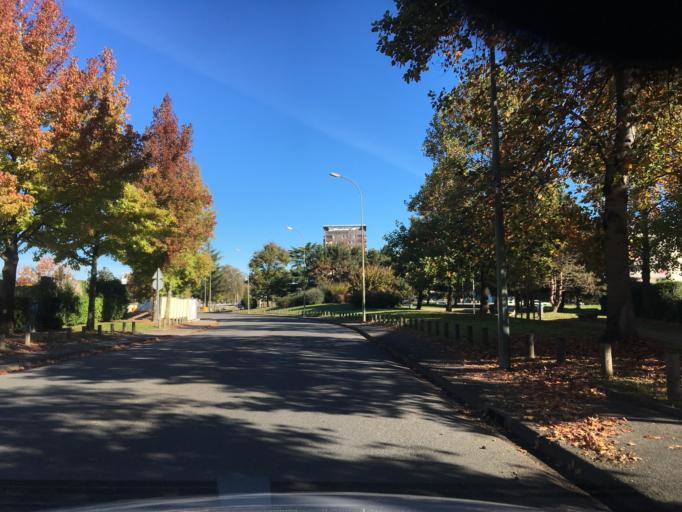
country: FR
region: Aquitaine
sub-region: Departement des Pyrenees-Atlantiques
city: Pau
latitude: 43.3180
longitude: -0.3437
